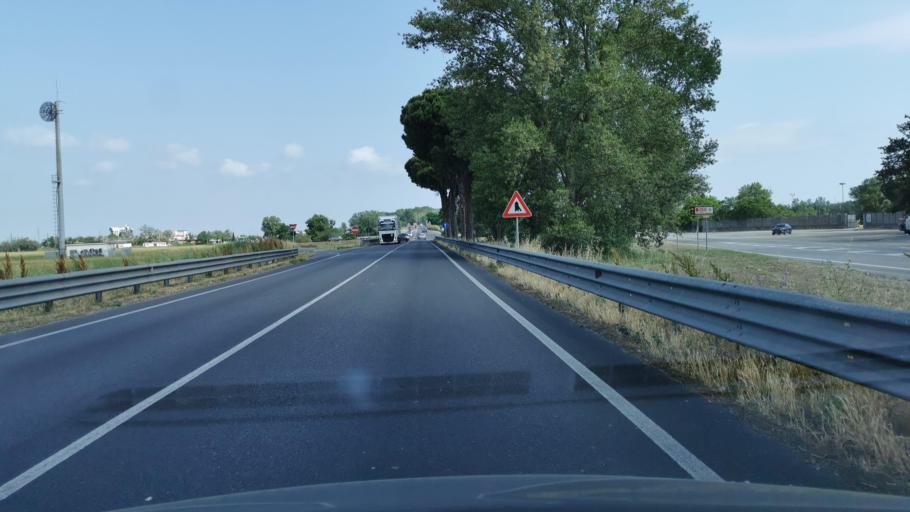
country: IT
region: Emilia-Romagna
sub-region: Provincia di Ferrara
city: Porto Garibaldi
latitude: 44.6714
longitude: 12.2298
